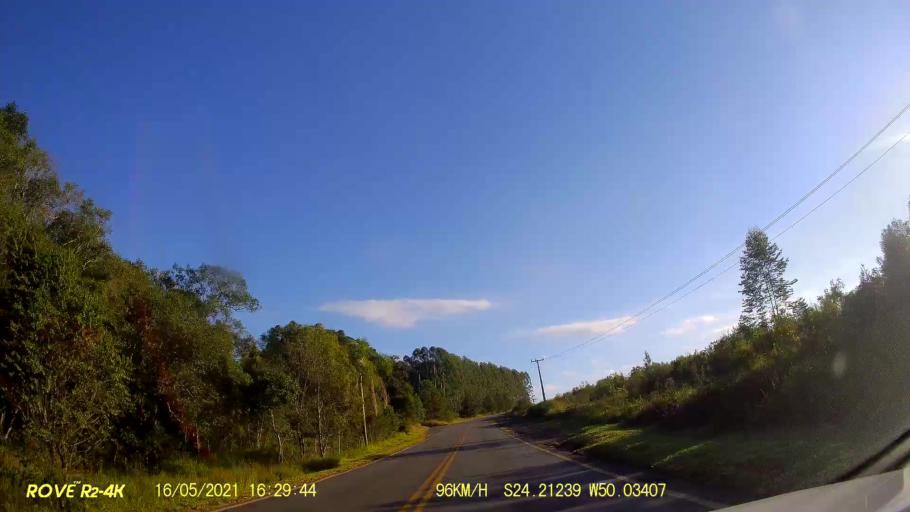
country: BR
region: Parana
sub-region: Pirai Do Sul
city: Pirai do Sul
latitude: -24.2125
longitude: -50.0342
